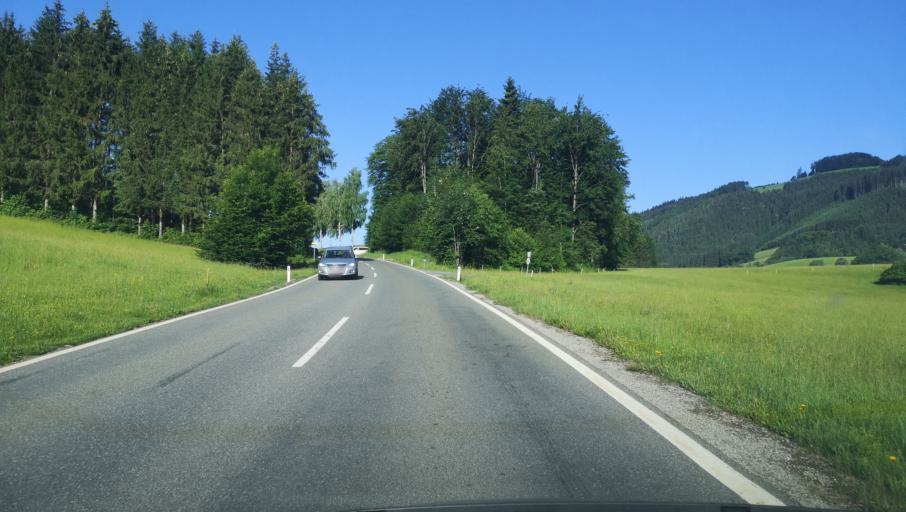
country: AT
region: Lower Austria
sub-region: Politischer Bezirk Scheibbs
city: Gresten
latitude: 47.9862
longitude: 15.0167
